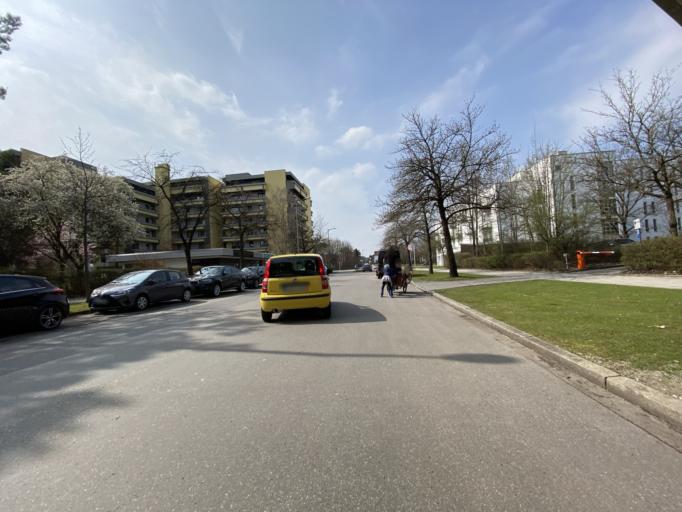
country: DE
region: Bavaria
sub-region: Upper Bavaria
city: Unterfoehring
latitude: 48.2007
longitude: 11.6133
